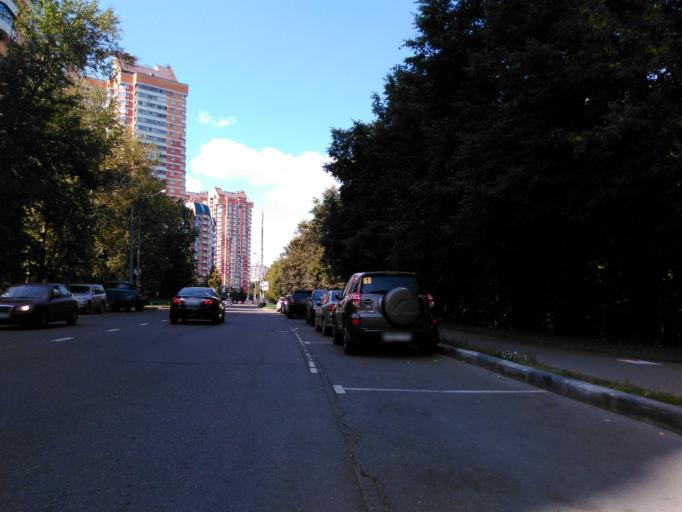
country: RU
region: Moscow
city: Ramenki
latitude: 55.6725
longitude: 37.5167
